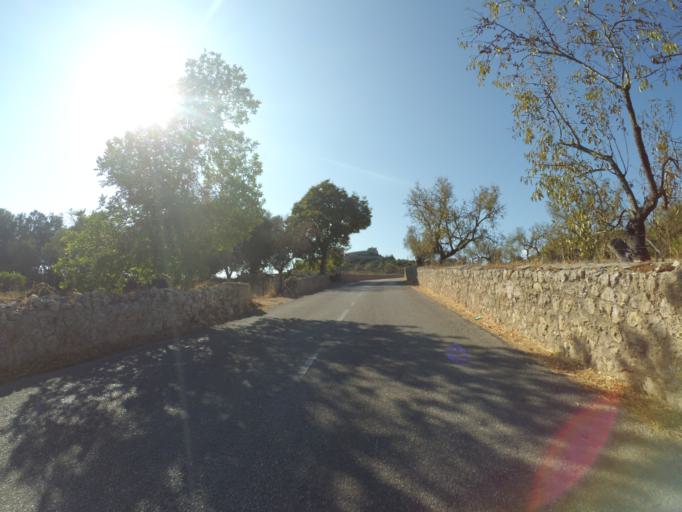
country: ES
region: Balearic Islands
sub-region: Illes Balears
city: Arta
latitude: 39.6998
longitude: 3.3517
